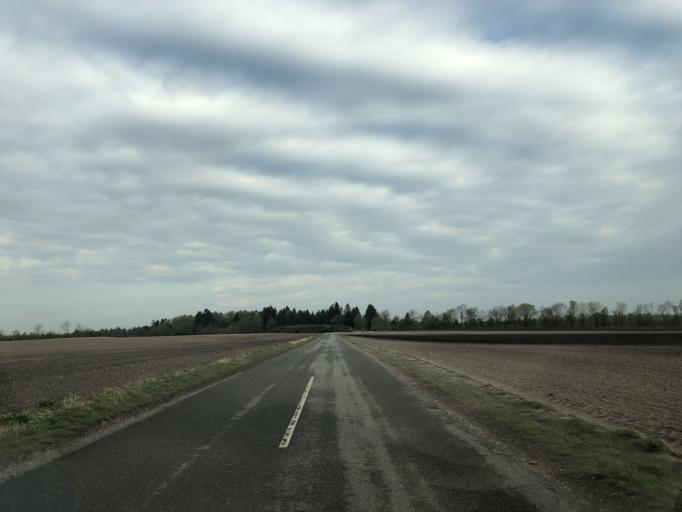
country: DK
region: Central Jutland
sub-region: Holstebro Kommune
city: Holstebro
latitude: 56.3117
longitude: 8.5284
